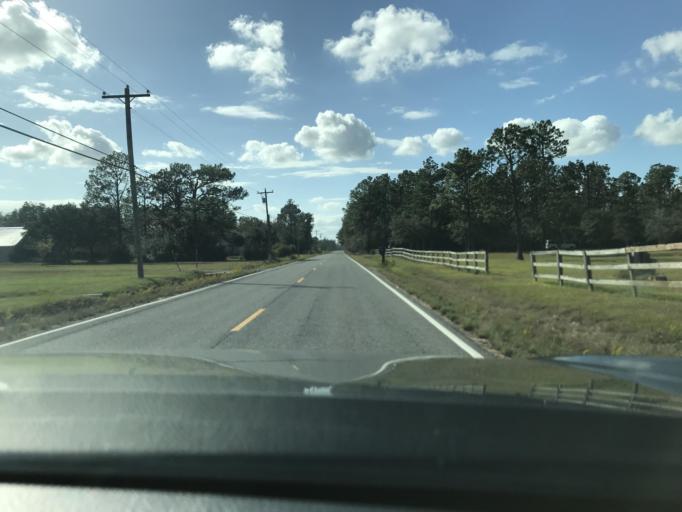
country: US
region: Louisiana
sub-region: Calcasieu Parish
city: Moss Bluff
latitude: 30.3226
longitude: -93.2668
